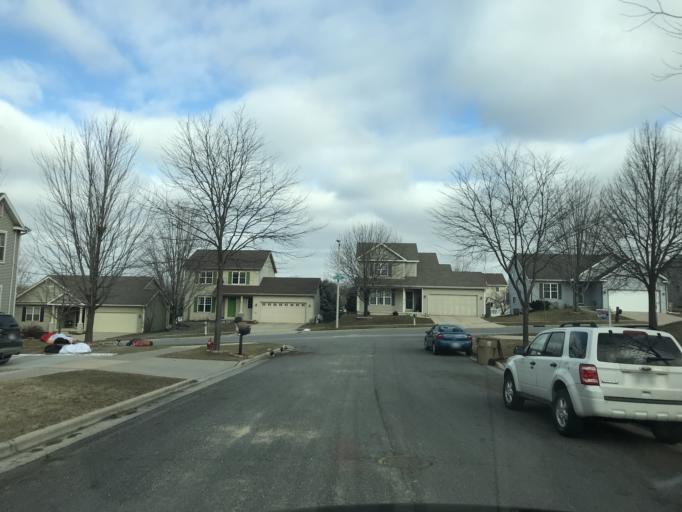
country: US
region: Wisconsin
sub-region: Dane County
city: Monona
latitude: 43.1108
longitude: -89.2898
